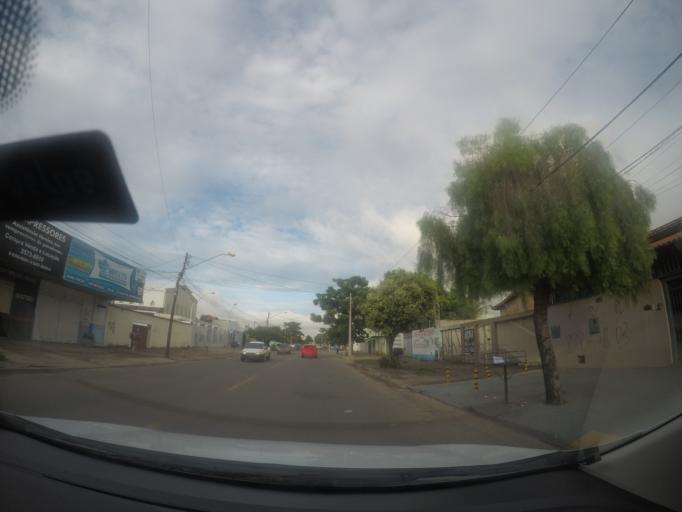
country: BR
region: Goias
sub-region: Goiania
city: Goiania
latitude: -16.6868
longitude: -49.3104
